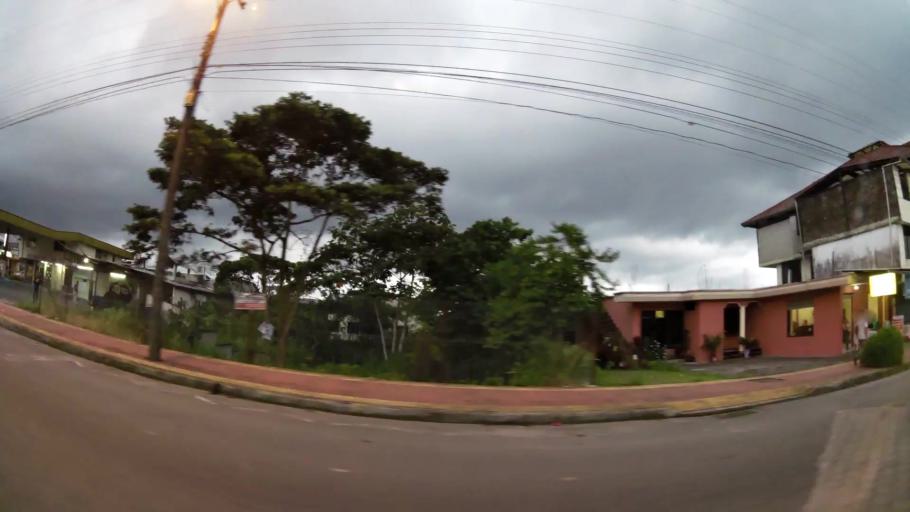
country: EC
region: Pastaza
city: Puyo
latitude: -1.4888
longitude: -78.0098
